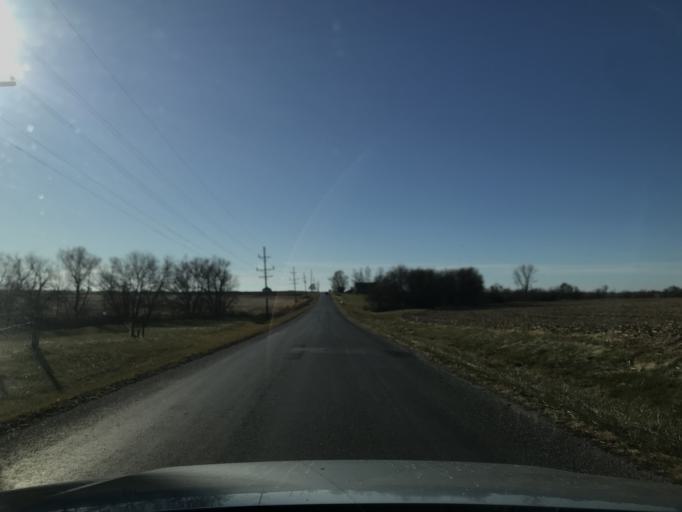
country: US
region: Illinois
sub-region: Hancock County
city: Carthage
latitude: 40.4898
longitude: -91.1779
